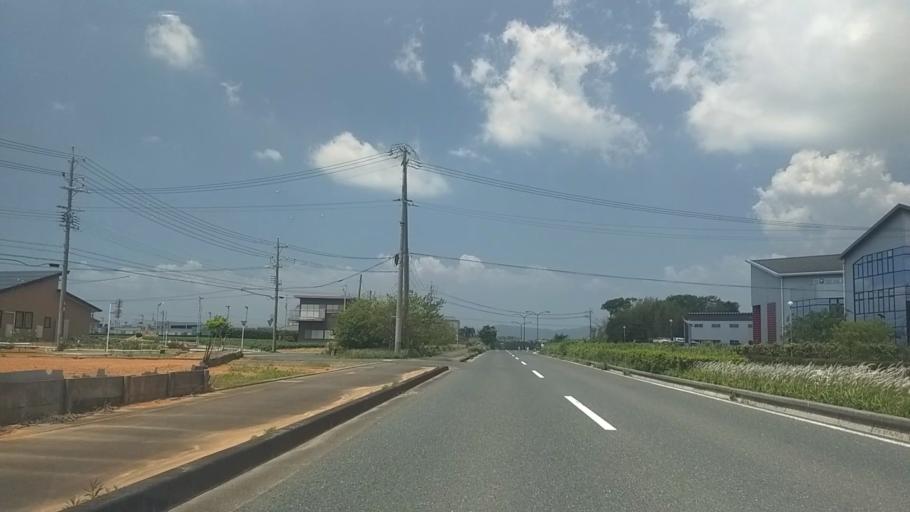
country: JP
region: Shizuoka
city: Hamamatsu
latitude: 34.7696
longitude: 137.6872
